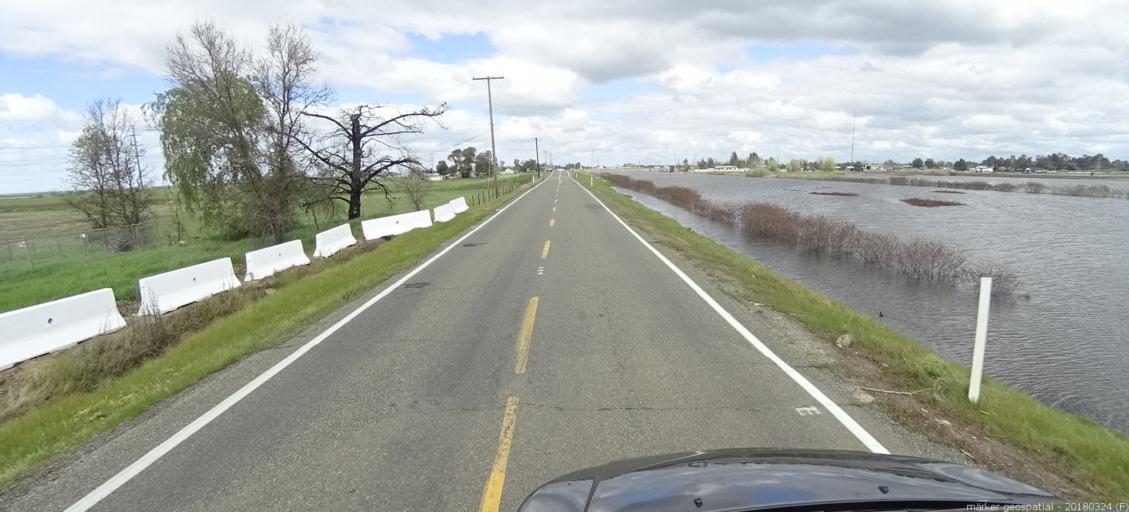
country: US
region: California
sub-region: Sacramento County
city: Elverta
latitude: 38.6948
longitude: -121.4856
